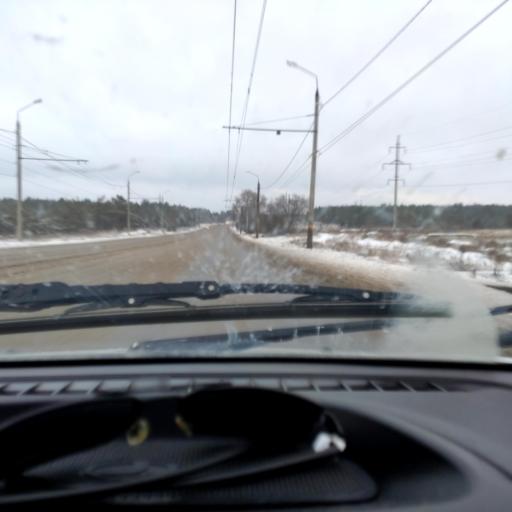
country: RU
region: Samara
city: Zhigulevsk
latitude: 53.5044
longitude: 49.5160
